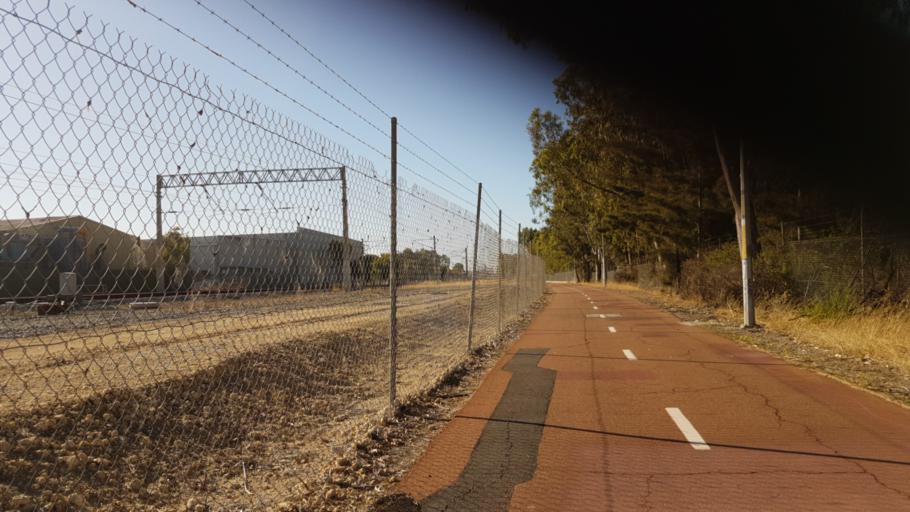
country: AU
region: Western Australia
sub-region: Gosnells
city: Kenwick
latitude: -32.0383
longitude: 115.9720
